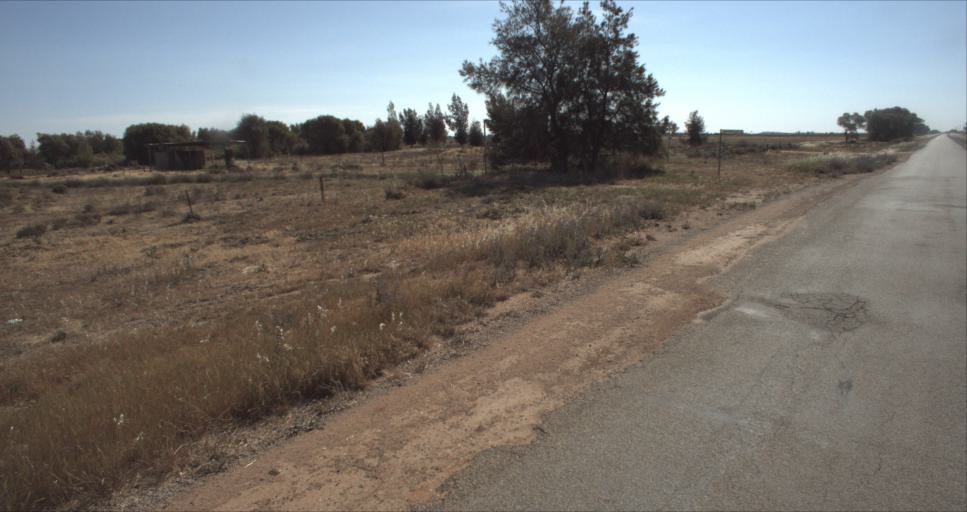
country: AU
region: New South Wales
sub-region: Leeton
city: Leeton
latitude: -34.4873
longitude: 146.3788
